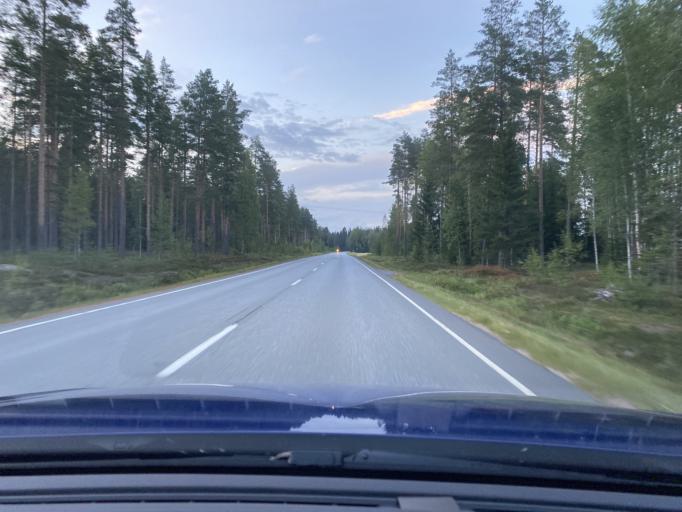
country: FI
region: Satakunta
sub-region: Pohjois-Satakunta
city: Honkajoki
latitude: 62.0483
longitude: 22.2465
